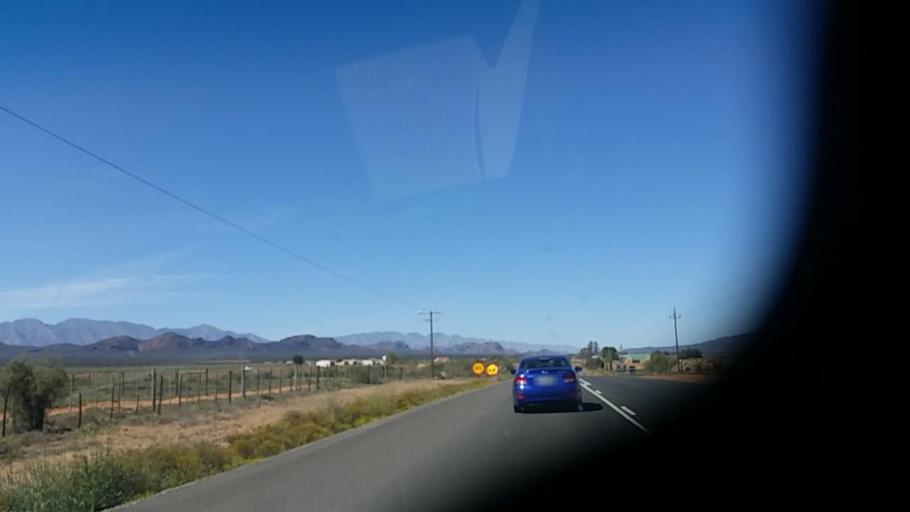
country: ZA
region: Western Cape
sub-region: Eden District Municipality
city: Oudtshoorn
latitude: -33.5832
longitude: 22.3044
